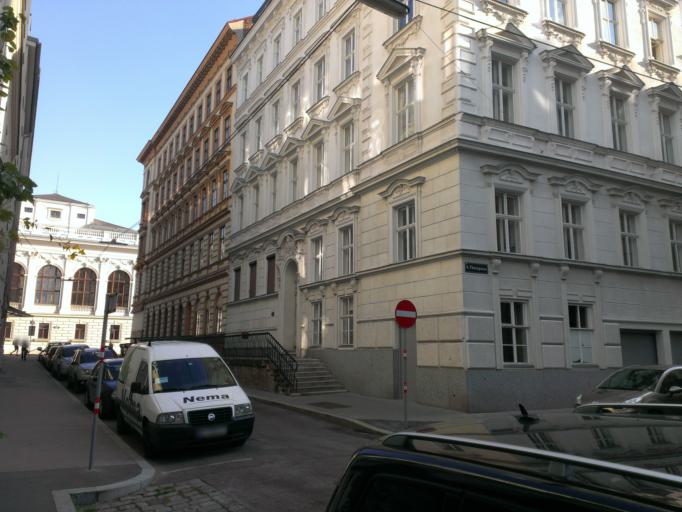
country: AT
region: Vienna
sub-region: Wien Stadt
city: Vienna
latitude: 48.2256
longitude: 16.3584
